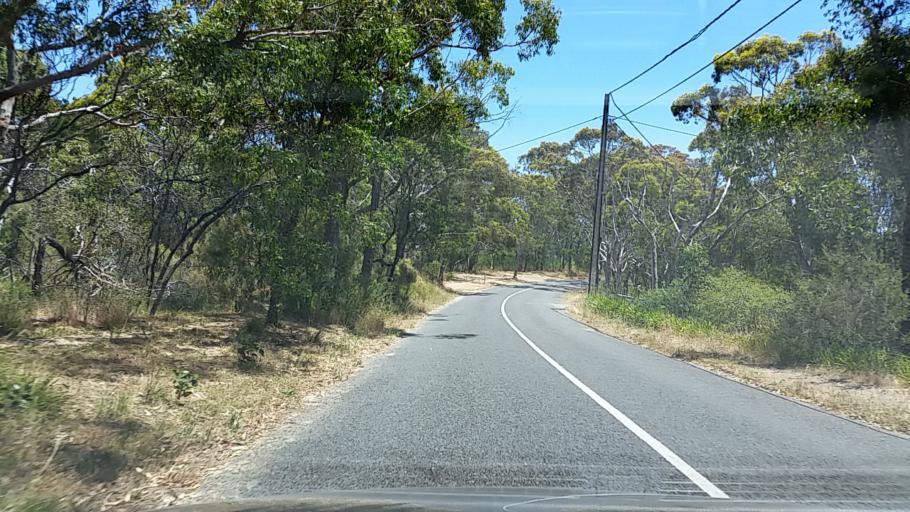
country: AU
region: South Australia
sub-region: Adelaide Hills
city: Crafers
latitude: -34.9914
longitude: 138.6791
